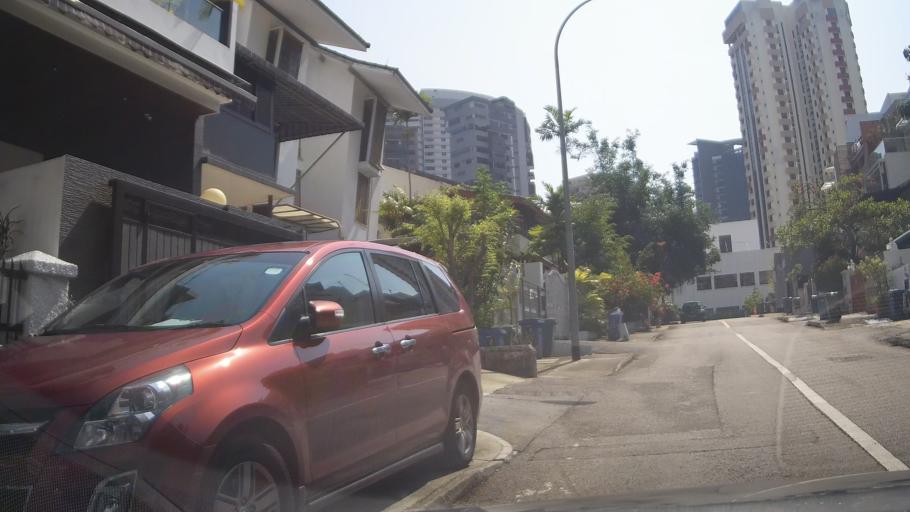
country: SG
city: Singapore
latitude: 1.3053
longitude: 103.8342
